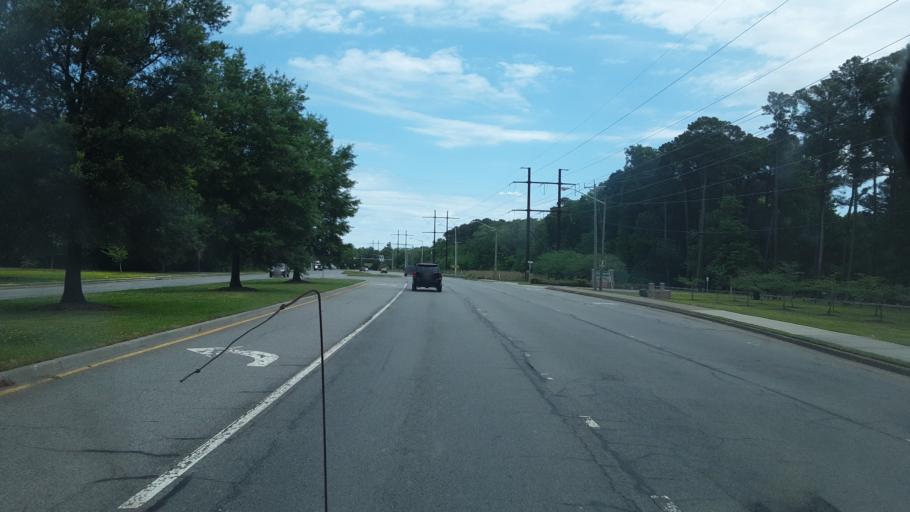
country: US
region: Virginia
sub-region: City of Virginia Beach
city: Virginia Beach
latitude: 36.7907
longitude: -75.9966
